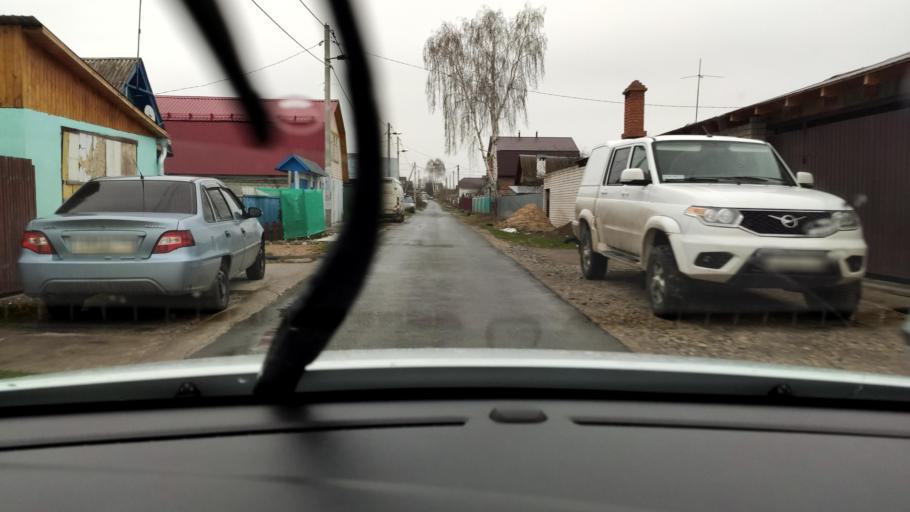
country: RU
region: Tatarstan
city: Osinovo
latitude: 55.8284
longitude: 48.8665
